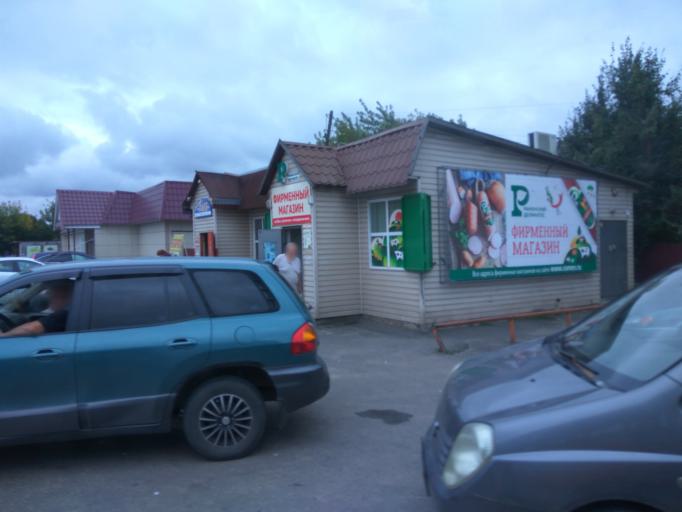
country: RU
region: Moskovskaya
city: Malyshevo
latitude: 55.4980
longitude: 38.3620
